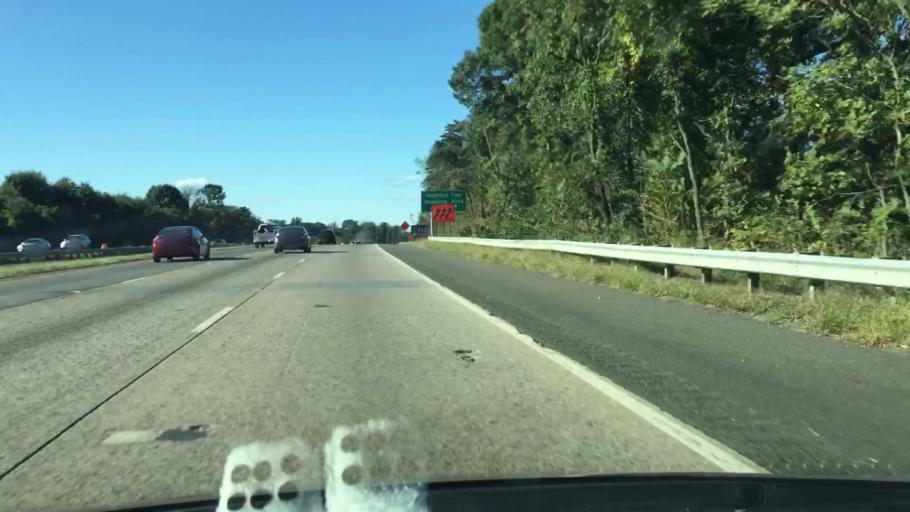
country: US
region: New Jersey
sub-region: Camden County
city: Glendora
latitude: 39.8218
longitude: -75.0776
